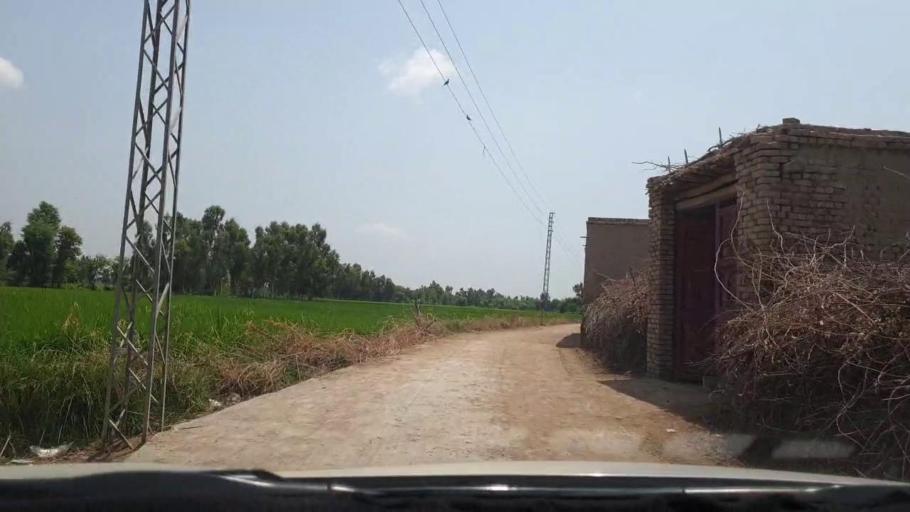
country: PK
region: Sindh
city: New Badah
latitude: 27.2972
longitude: 68.0705
